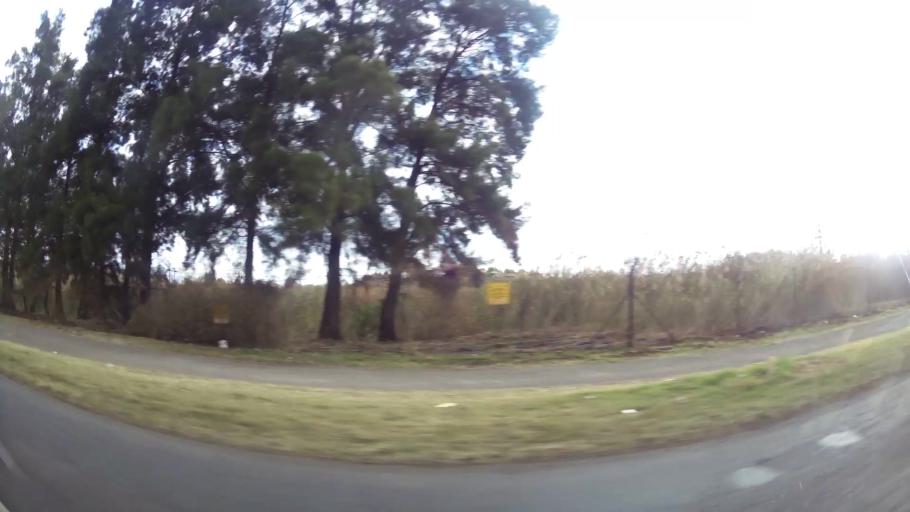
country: ZA
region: Orange Free State
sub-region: Fezile Dabi District Municipality
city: Sasolburg
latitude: -26.8261
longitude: 27.8375
